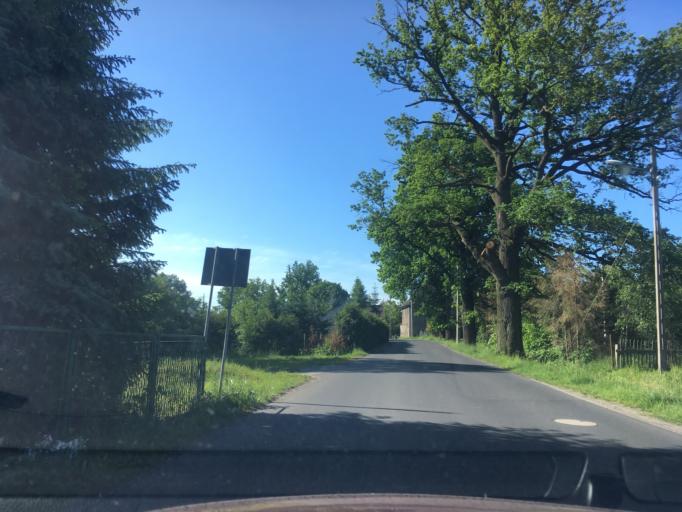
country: PL
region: Lower Silesian Voivodeship
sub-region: Powiat zgorzelecki
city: Sulikow
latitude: 51.0815
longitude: 15.0569
